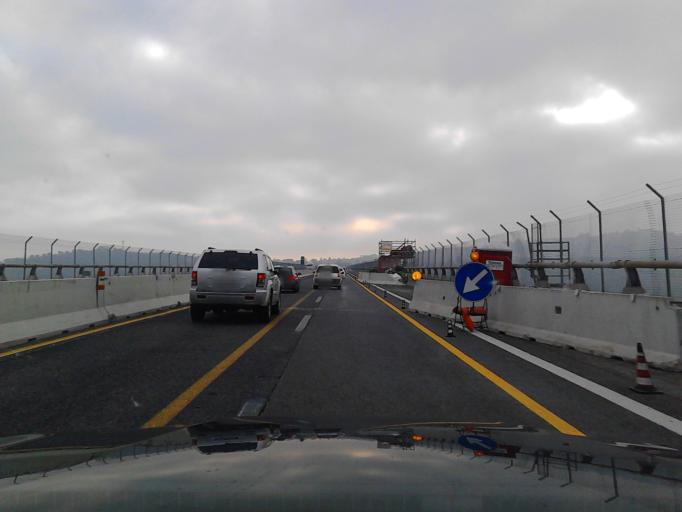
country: IT
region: Abruzzo
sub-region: Provincia di Teramo
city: Tortoreto Lido
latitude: 42.7814
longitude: 13.9340
